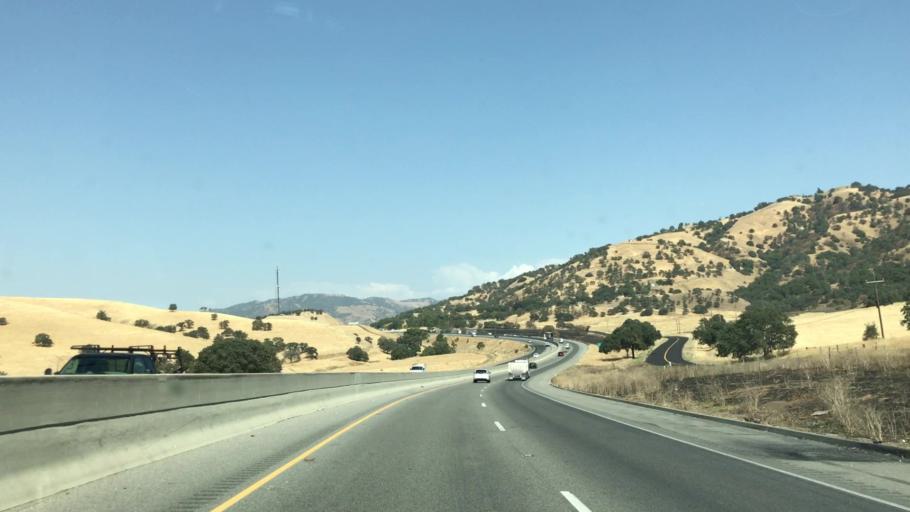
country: US
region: California
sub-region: Kern County
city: Bear Valley Springs
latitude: 35.2638
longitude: -118.6465
